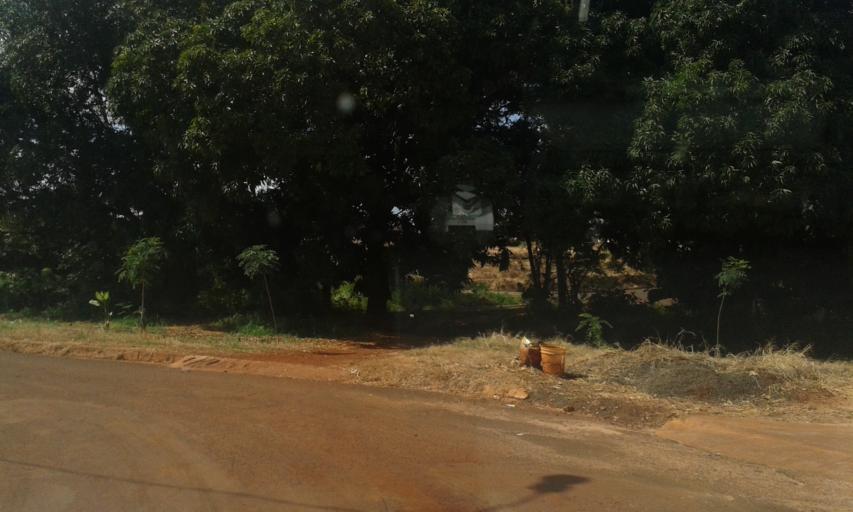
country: BR
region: Minas Gerais
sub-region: Capinopolis
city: Capinopolis
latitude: -18.6888
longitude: -49.5719
